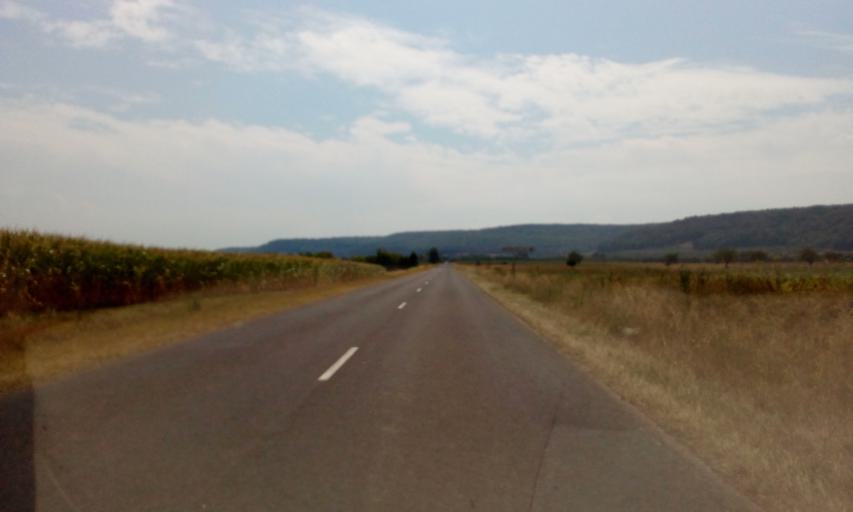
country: FR
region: Lorraine
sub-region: Departement de la Meuse
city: Vigneulles-les-Hattonchatel
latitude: 49.0556
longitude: 5.6497
